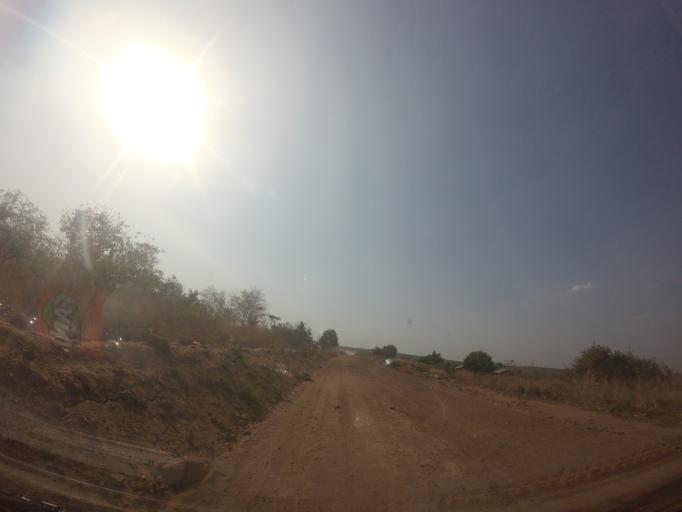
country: UG
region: Northern Region
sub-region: Maracha District
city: Maracha
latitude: 3.1052
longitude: 31.2072
